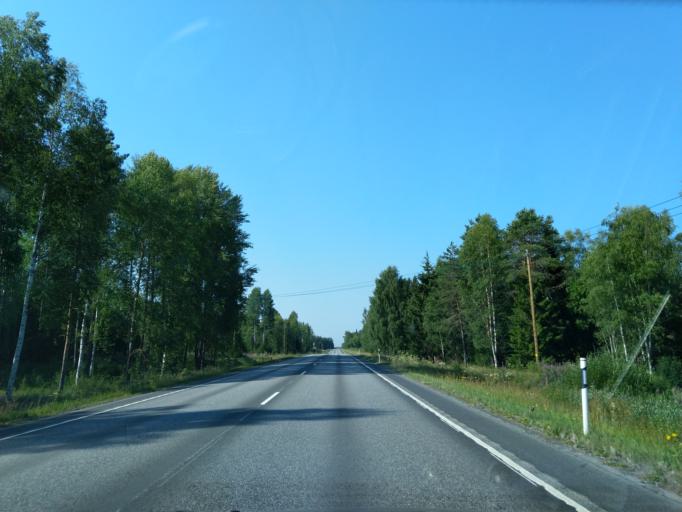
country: FI
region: Satakunta
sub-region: Pori
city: Pomarkku
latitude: 61.7324
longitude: 22.0751
